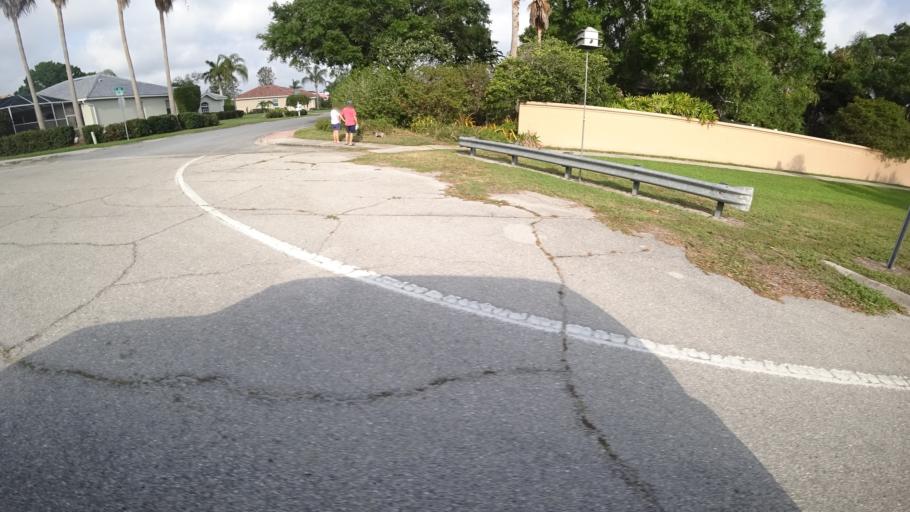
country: US
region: Florida
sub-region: Sarasota County
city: North Sarasota
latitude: 27.4134
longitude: -82.5135
